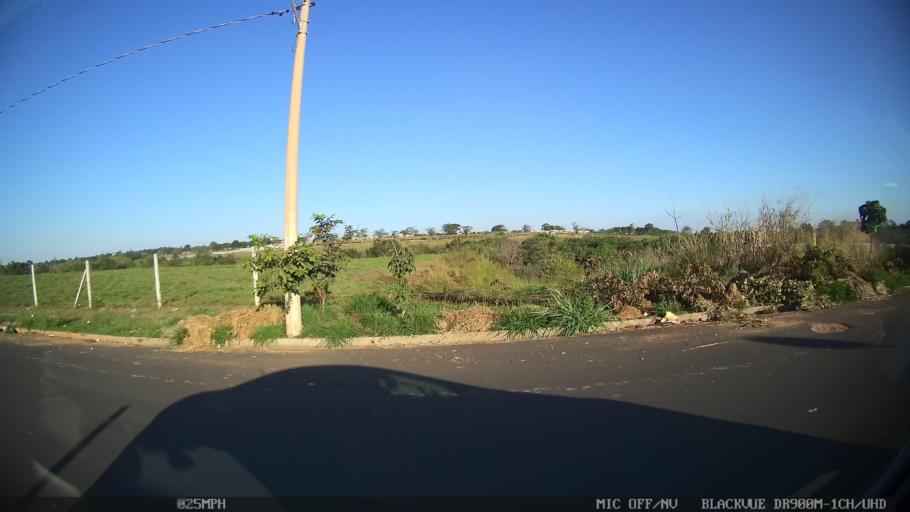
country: BR
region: Sao Paulo
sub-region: Nova Odessa
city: Nova Odessa
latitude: -22.7790
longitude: -47.2765
